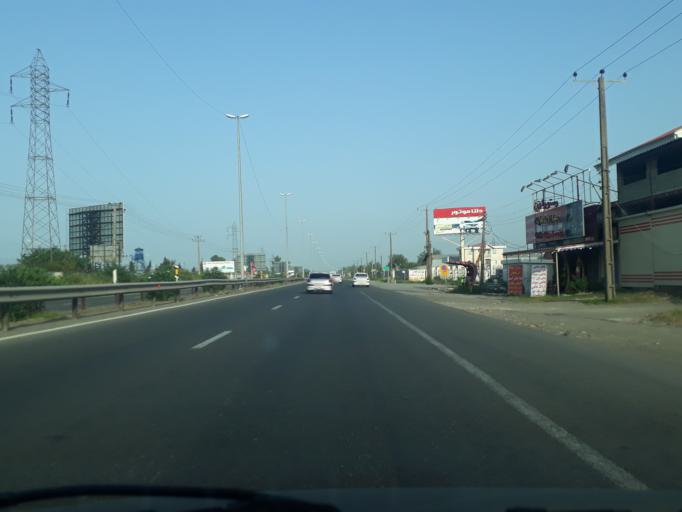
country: IR
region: Gilan
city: Bandar-e Anzali
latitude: 37.4599
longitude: 49.5902
